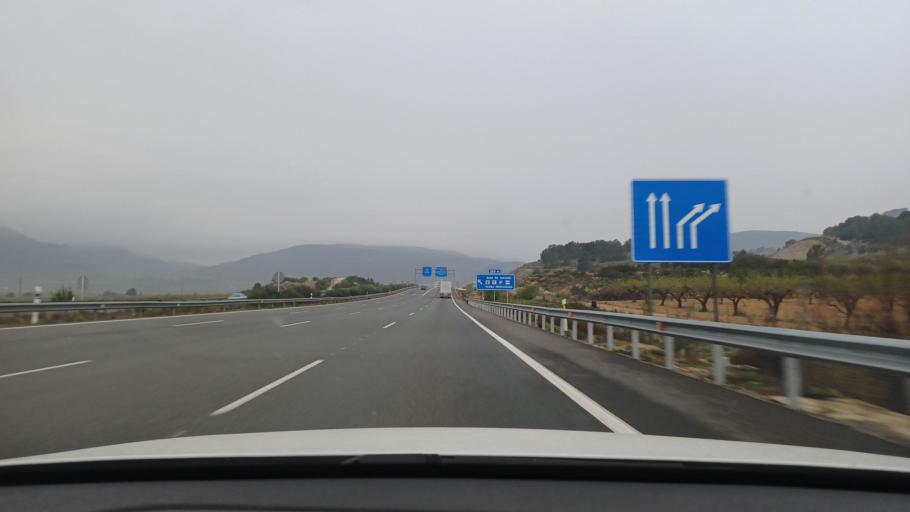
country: ES
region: Valencia
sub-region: Provincia de Valencia
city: La Font de la Figuera
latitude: 38.8318
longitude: -0.8783
